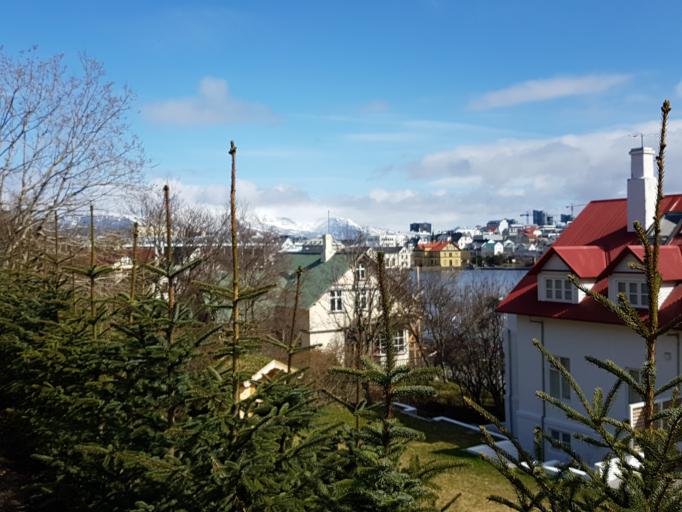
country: IS
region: Capital Region
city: Kopavogur
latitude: 64.1443
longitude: -21.9463
